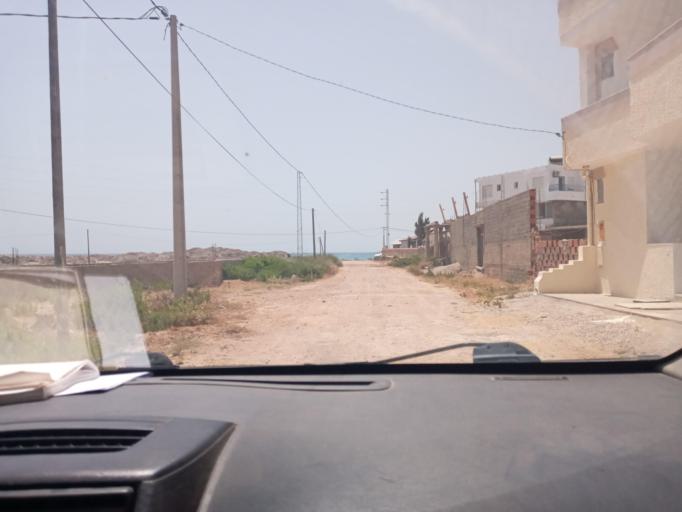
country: TN
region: Nabul
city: El Haouaria
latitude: 37.0420
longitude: 11.0618
